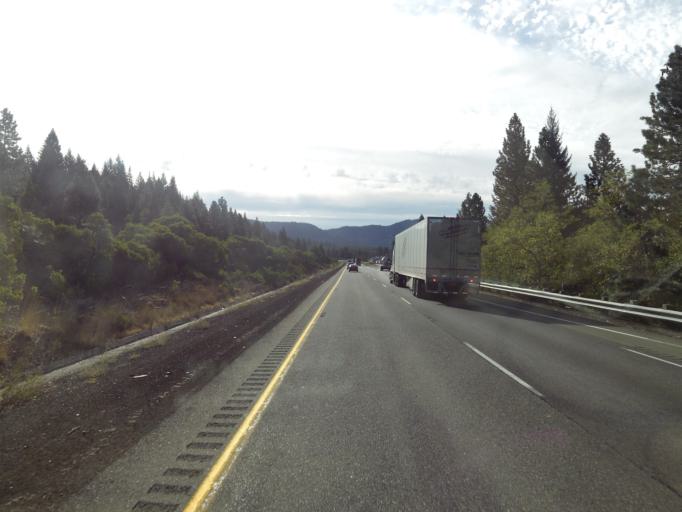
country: US
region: California
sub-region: Siskiyou County
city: Mount Shasta
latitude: 41.2756
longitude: -122.2862
